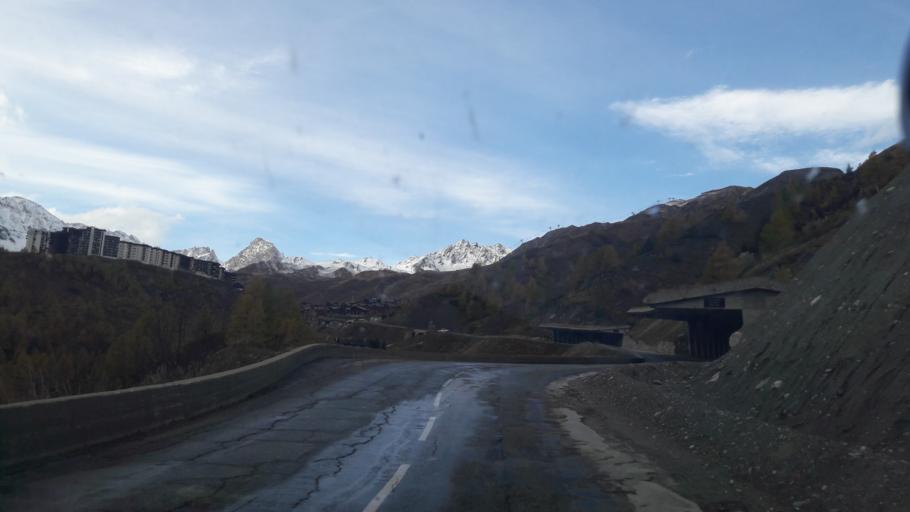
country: FR
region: Rhone-Alpes
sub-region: Departement de la Savoie
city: Tignes
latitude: 45.4779
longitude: 6.9226
